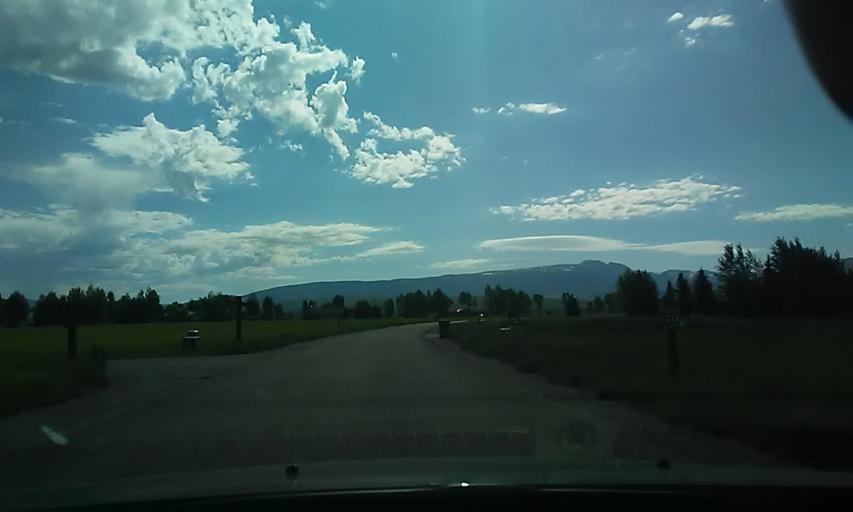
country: US
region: Wyoming
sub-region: Teton County
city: Jackson
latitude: 43.5776
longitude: -110.7503
